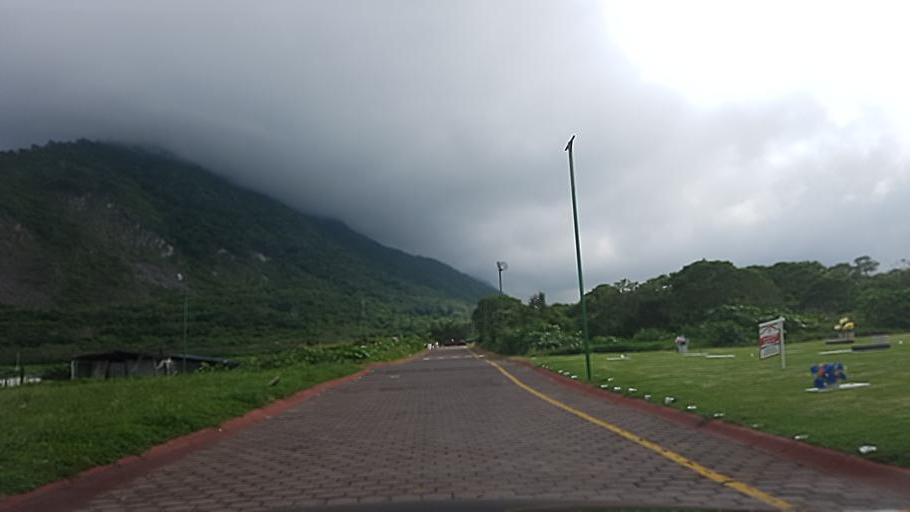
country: MX
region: Nayarit
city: Tepic
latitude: 21.5186
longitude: -104.9302
